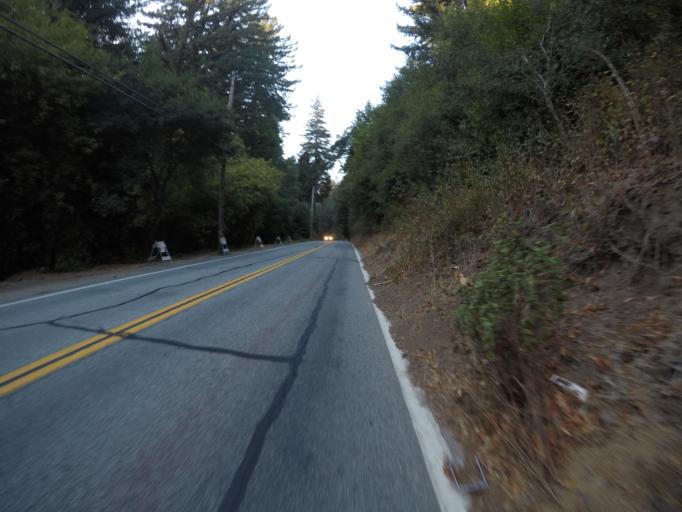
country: US
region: California
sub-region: Santa Cruz County
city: Pasatiempo
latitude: 36.9954
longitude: -122.0358
